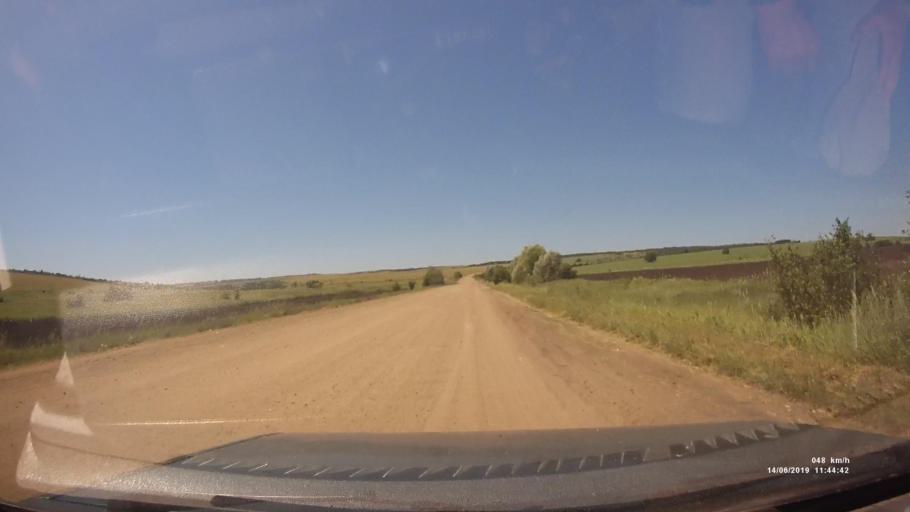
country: RU
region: Rostov
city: Kazanskaya
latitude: 49.8535
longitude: 41.3211
